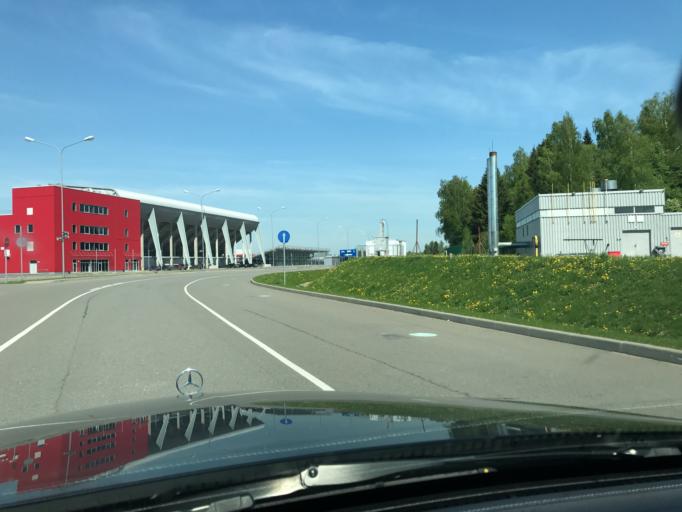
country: RU
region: Moskovskaya
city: Sychevo
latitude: 55.9933
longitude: 36.2724
